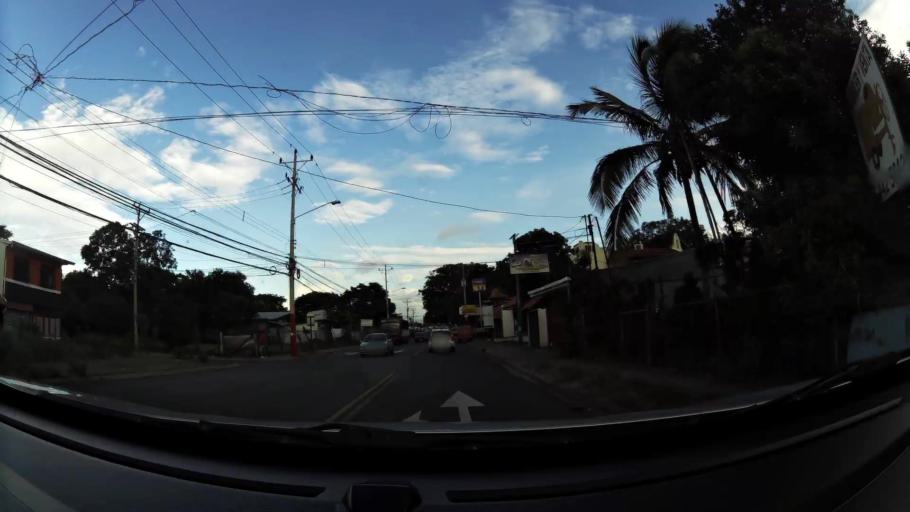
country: CR
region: Alajuela
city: Alajuela
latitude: 10.0009
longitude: -84.1986
